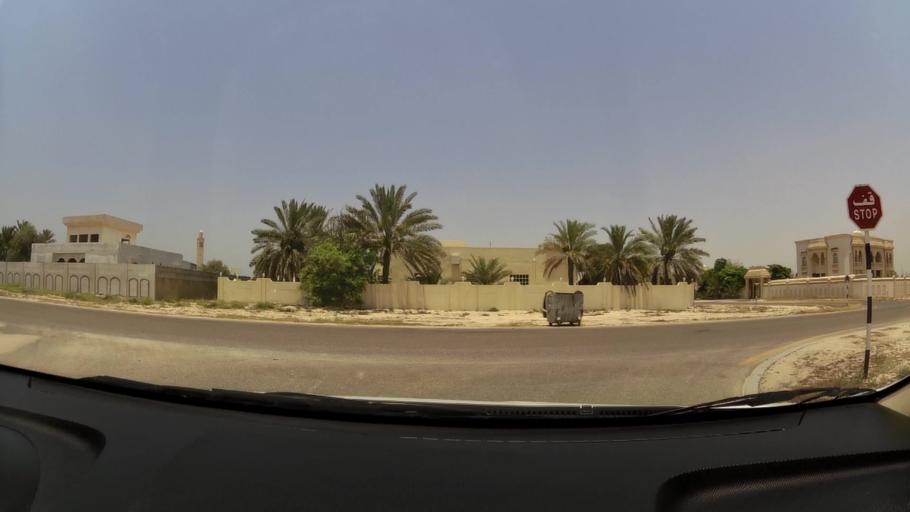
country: AE
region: Umm al Qaywayn
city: Umm al Qaywayn
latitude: 25.5450
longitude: 55.5397
